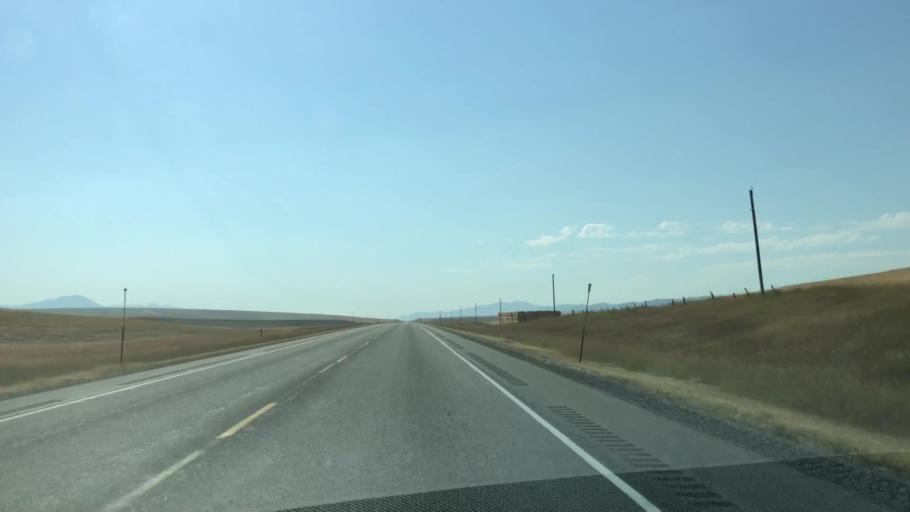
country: US
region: Idaho
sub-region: Madison County
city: Rexburg
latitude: 43.5420
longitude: -111.5192
